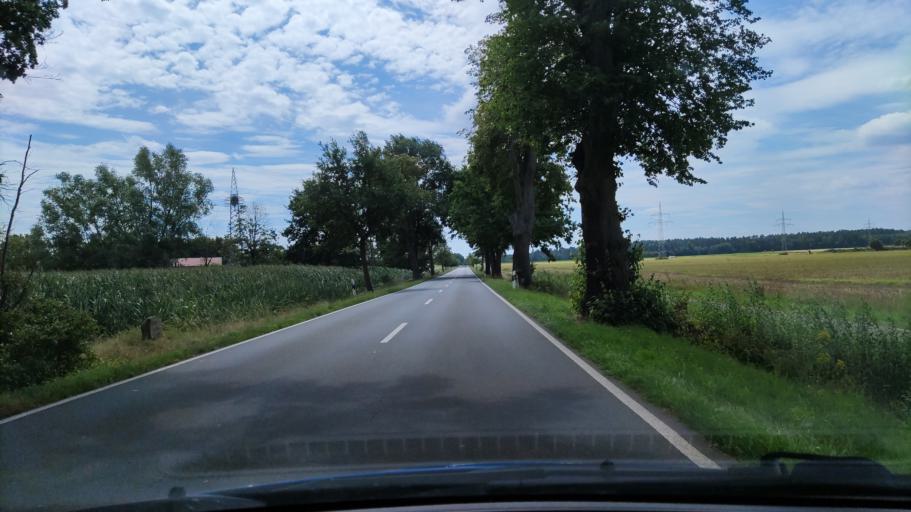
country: DE
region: Lower Saxony
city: Clenze
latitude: 52.9269
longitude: 10.9497
